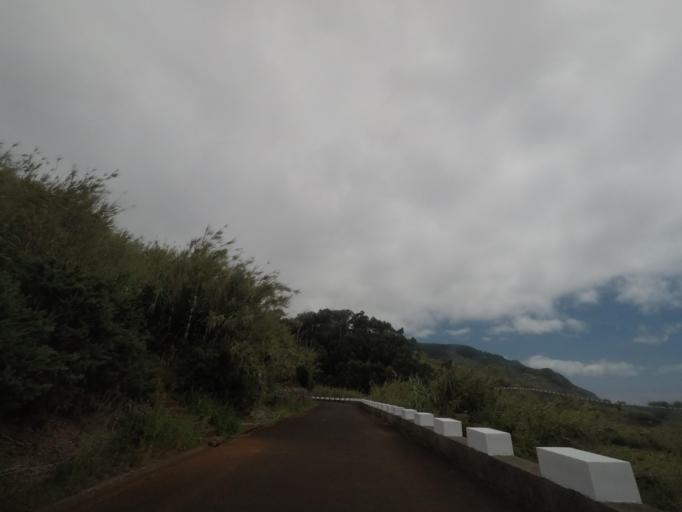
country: PT
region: Madeira
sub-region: Porto Moniz
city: Porto Moniz
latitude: 32.8608
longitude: -17.2011
